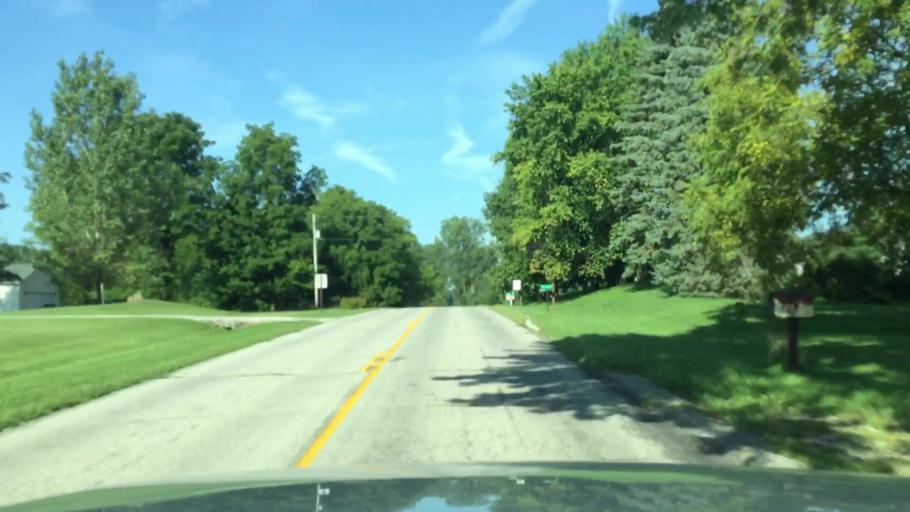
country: US
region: Michigan
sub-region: Lenawee County
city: Manitou Beach-Devils Lake
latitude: 41.9425
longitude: -84.3588
